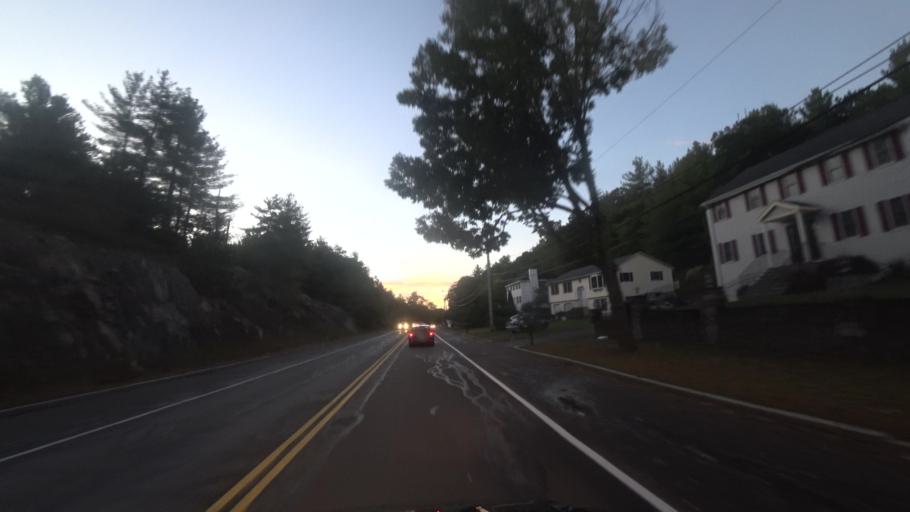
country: US
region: Massachusetts
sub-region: Middlesex County
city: Melrose
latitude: 42.4853
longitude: -71.0443
